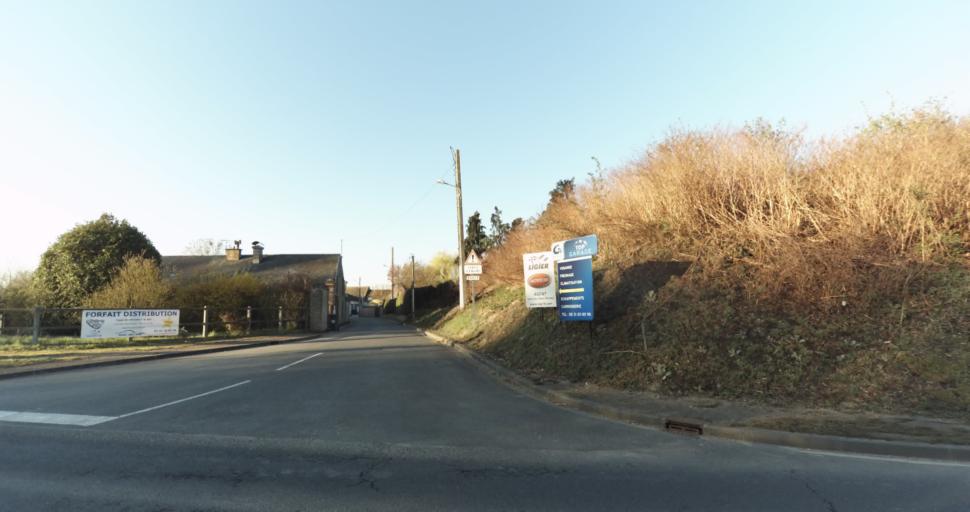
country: FR
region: Lower Normandy
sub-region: Departement du Calvados
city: Saint-Pierre-sur-Dives
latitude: 49.0203
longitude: -0.0442
